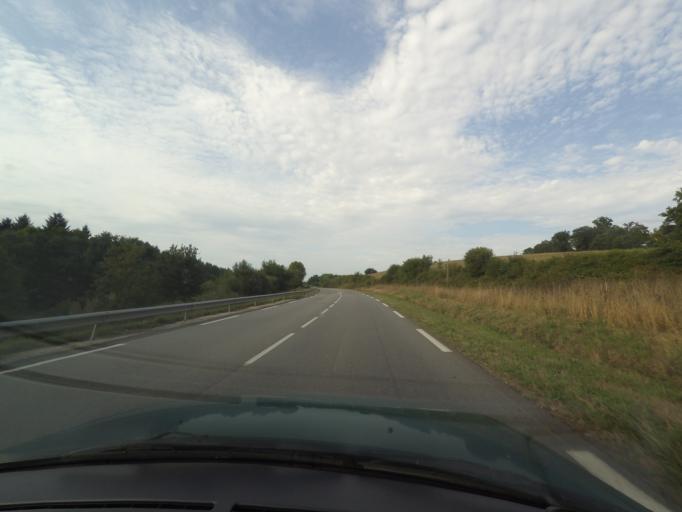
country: FR
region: Limousin
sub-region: Departement de la Haute-Vienne
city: Aixe-sur-Vienne
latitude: 45.7857
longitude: 1.1114
